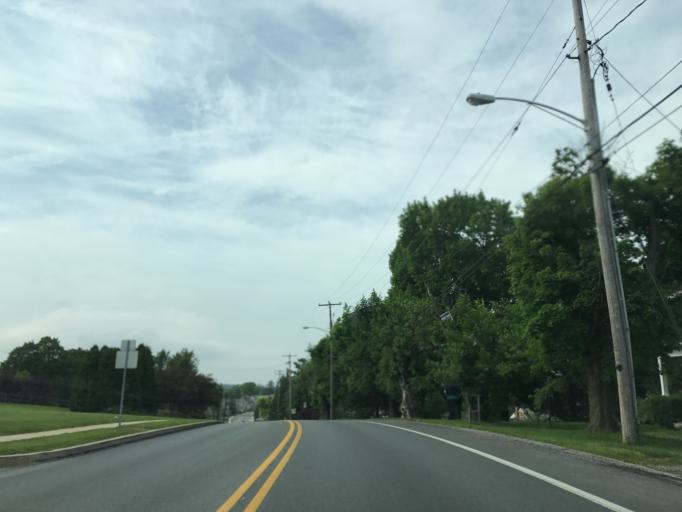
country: US
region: Pennsylvania
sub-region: York County
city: Spry
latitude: 39.9129
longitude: -76.6825
